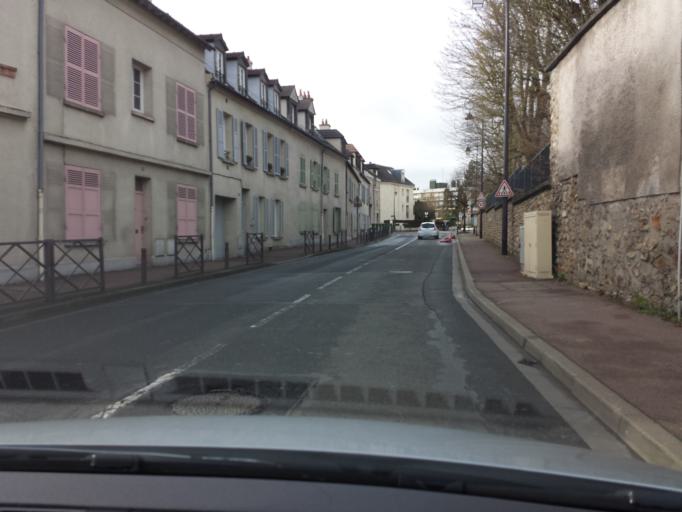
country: FR
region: Ile-de-France
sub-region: Departement des Hauts-de-Seine
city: Antony
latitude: 48.7548
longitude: 2.2946
